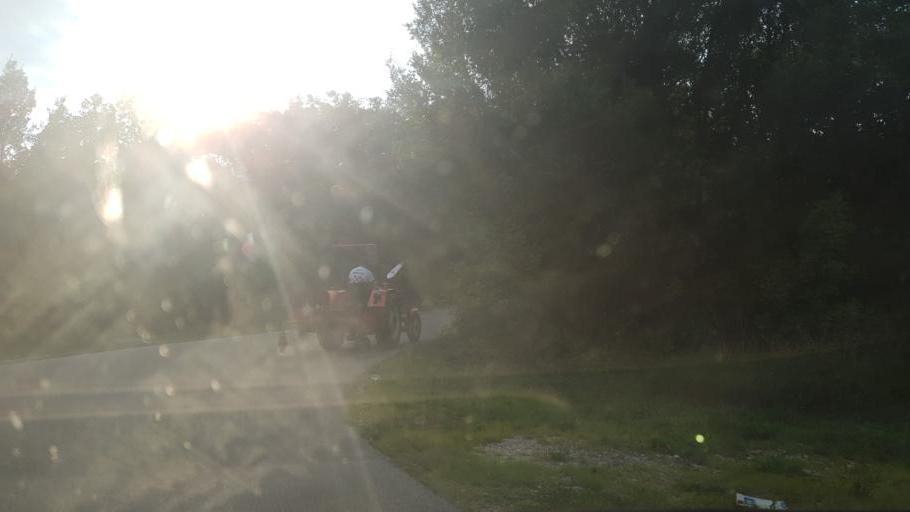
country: HR
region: Primorsko-Goranska
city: Njivice
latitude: 45.1436
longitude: 14.5828
